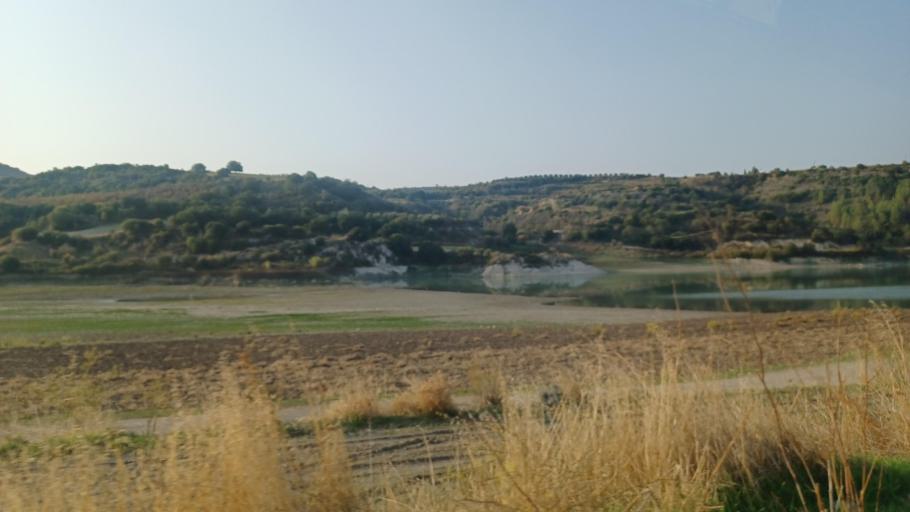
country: CY
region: Pafos
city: Polis
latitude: 34.9602
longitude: 32.4889
